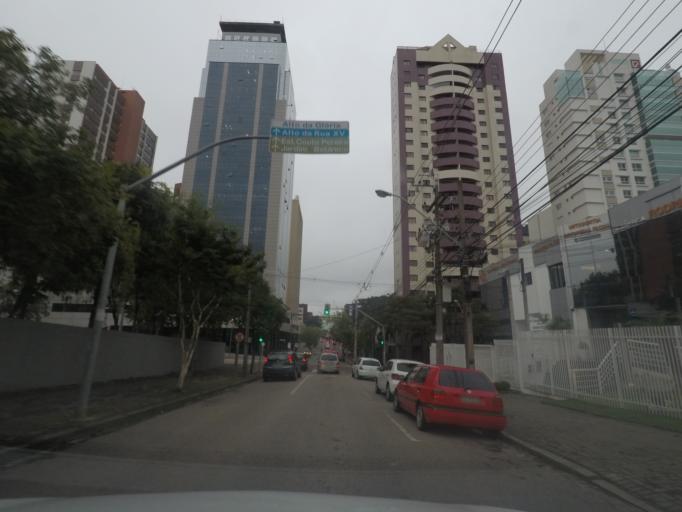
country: BR
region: Parana
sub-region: Curitiba
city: Curitiba
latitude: -25.4169
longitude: -49.2639
